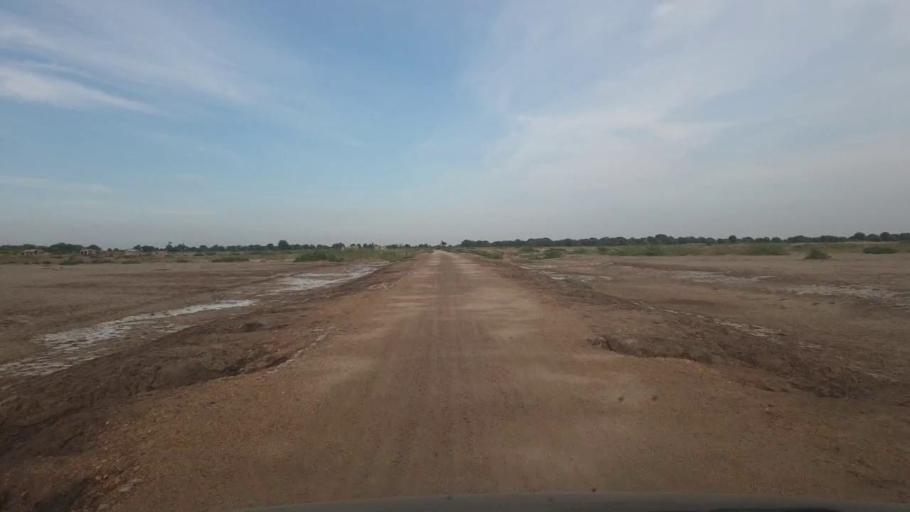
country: PK
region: Sindh
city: Kunri
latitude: 25.2970
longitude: 69.5746
